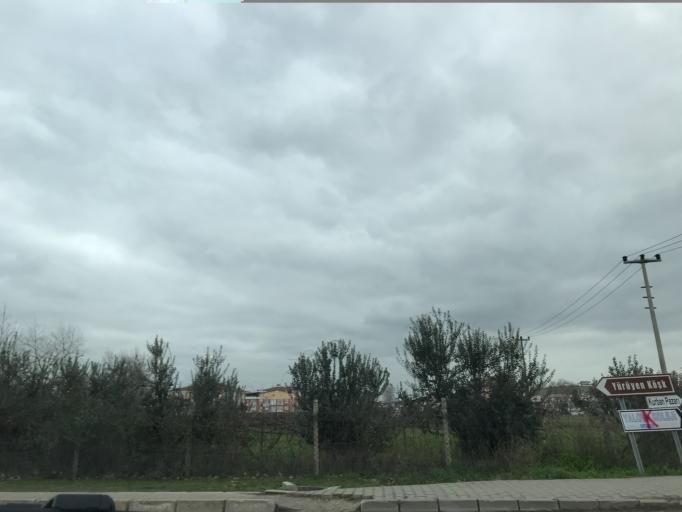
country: TR
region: Yalova
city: Ciftlikkoy
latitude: 40.6608
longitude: 29.3063
